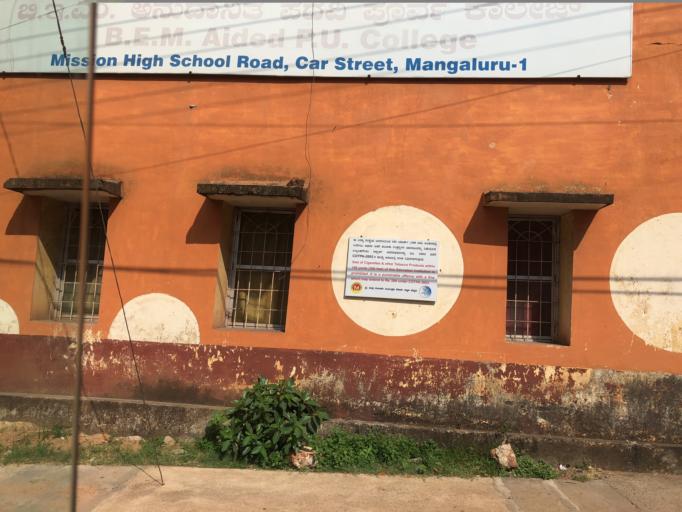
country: IN
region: Karnataka
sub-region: Dakshina Kannada
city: Mangalore
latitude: 12.8716
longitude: 74.8349
